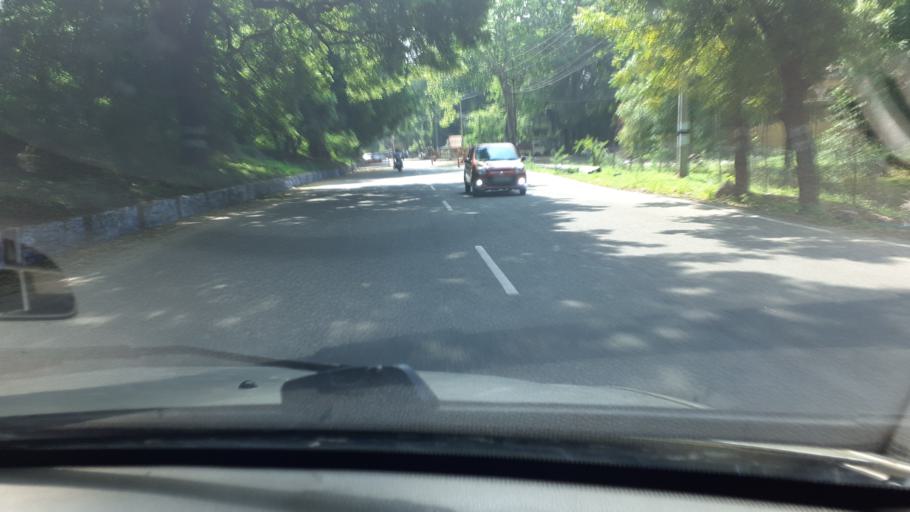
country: IN
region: Tamil Nadu
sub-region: Thoothukkudi
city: Srivaikuntam
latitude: 8.6273
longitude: 77.9073
